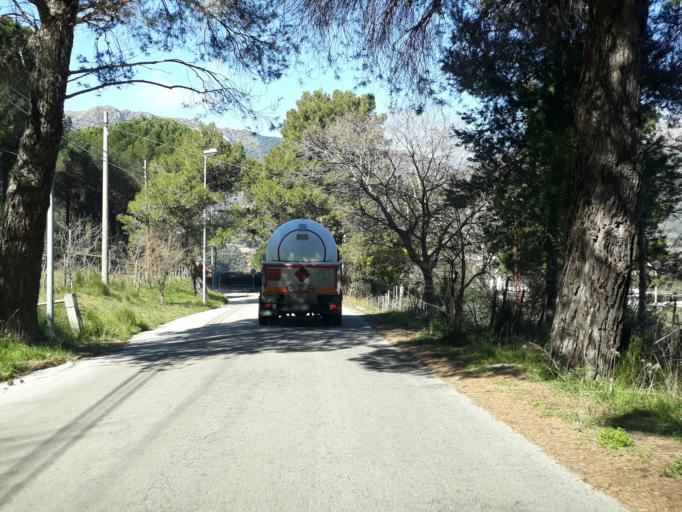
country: IT
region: Sicily
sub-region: Palermo
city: Piano dei Geli
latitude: 38.0848
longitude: 13.2678
